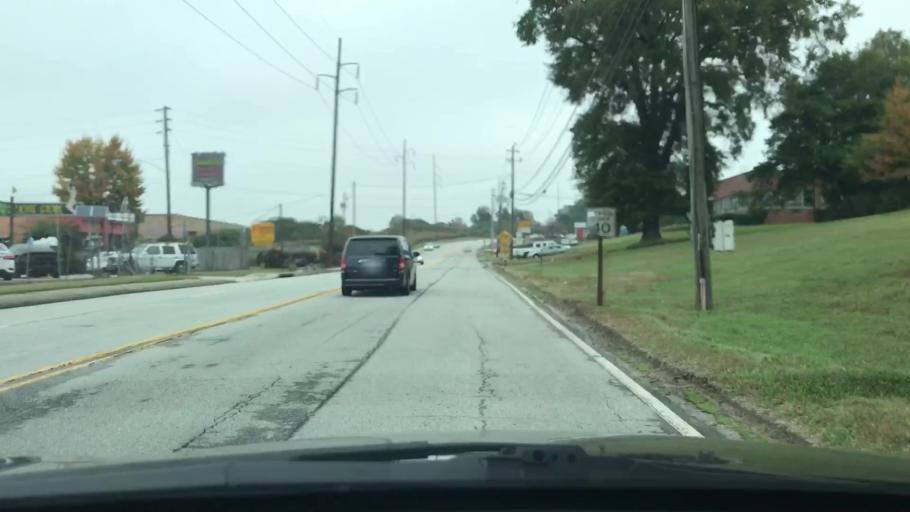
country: US
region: Georgia
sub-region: DeKalb County
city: Avondale Estates
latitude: 33.7819
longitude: -84.2738
